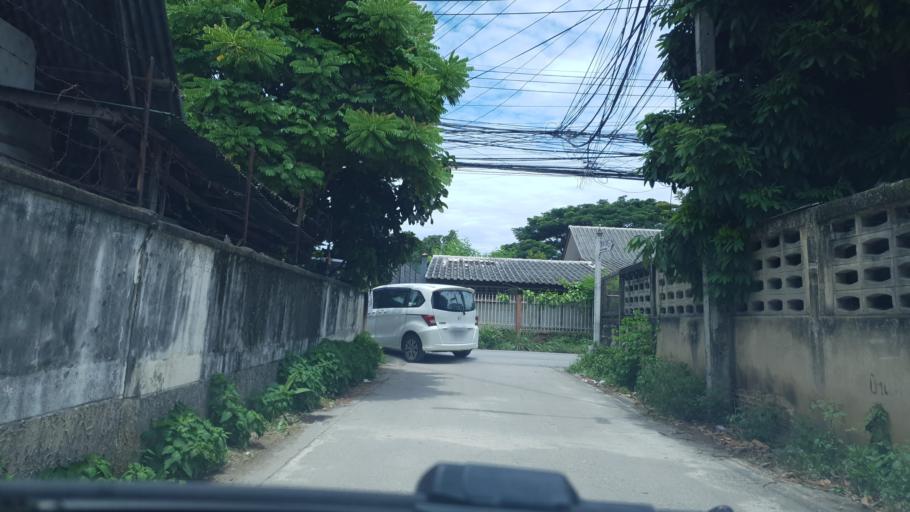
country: TH
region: Chiang Mai
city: Chiang Mai
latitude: 18.8036
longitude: 99.0028
